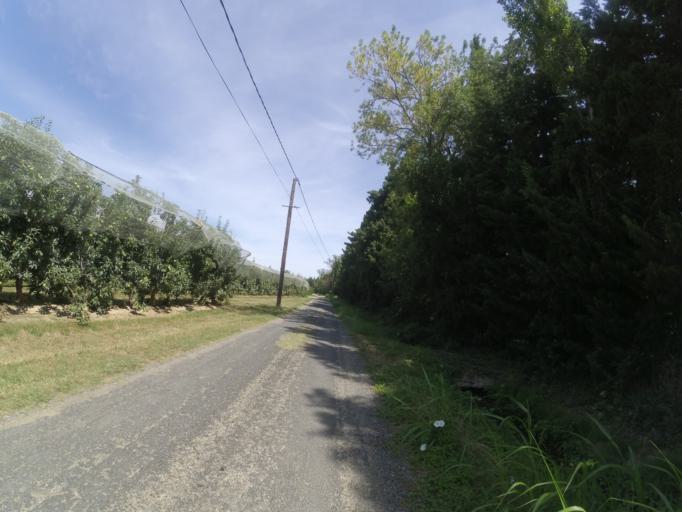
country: FR
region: Languedoc-Roussillon
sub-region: Departement des Pyrenees-Orientales
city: Millas
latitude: 42.6843
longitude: 2.6763
